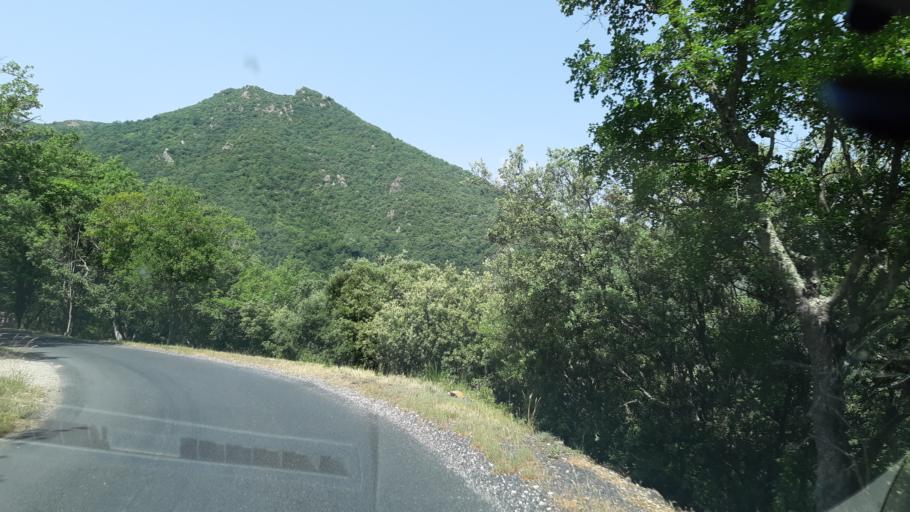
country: FR
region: Languedoc-Roussillon
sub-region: Departement des Pyrenees-Orientales
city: els Banys d'Arles
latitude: 42.5127
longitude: 2.6369
